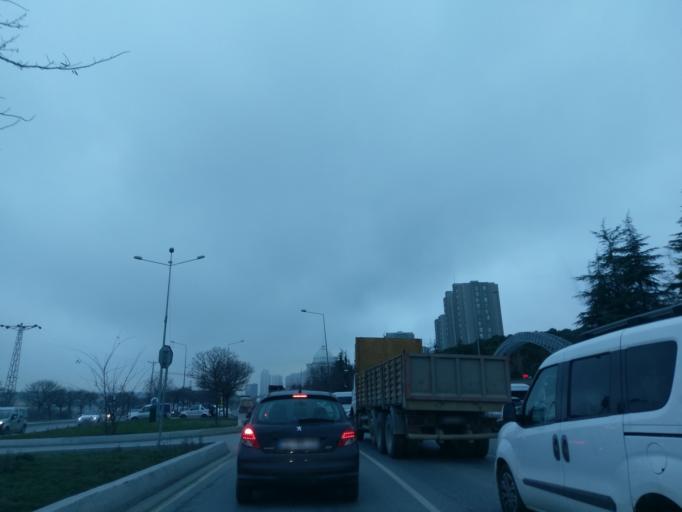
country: TR
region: Istanbul
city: Mahmutbey
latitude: 41.0465
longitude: 28.7743
